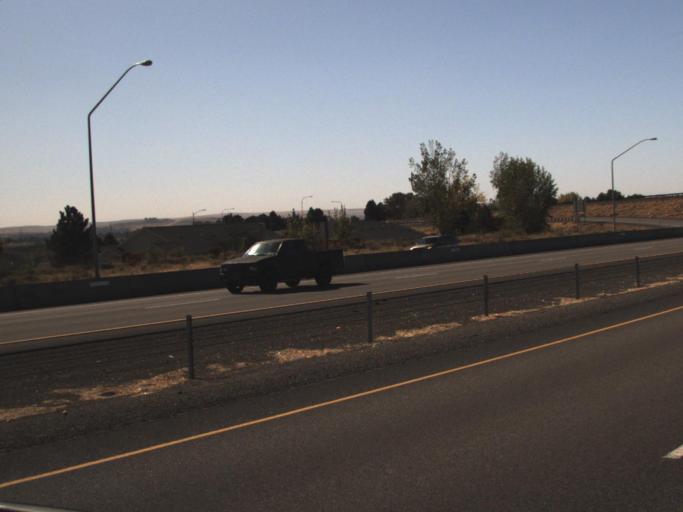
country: US
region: Washington
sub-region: Franklin County
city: Pasco
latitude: 46.2488
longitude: -119.1227
